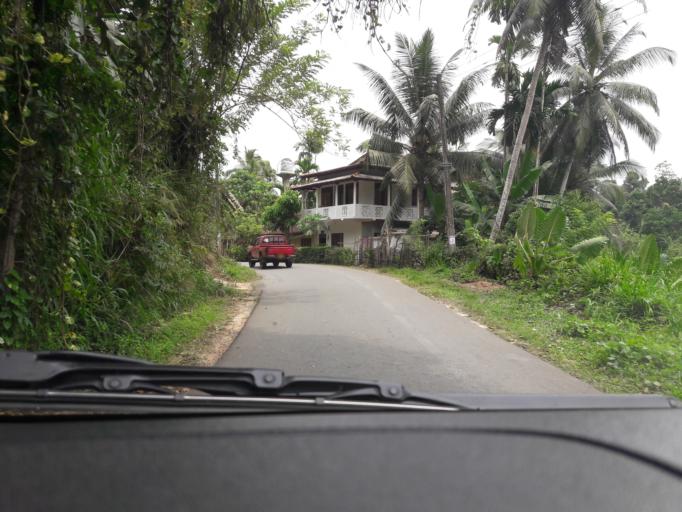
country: LK
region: Southern
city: Galle
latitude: 6.1797
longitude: 80.2903
